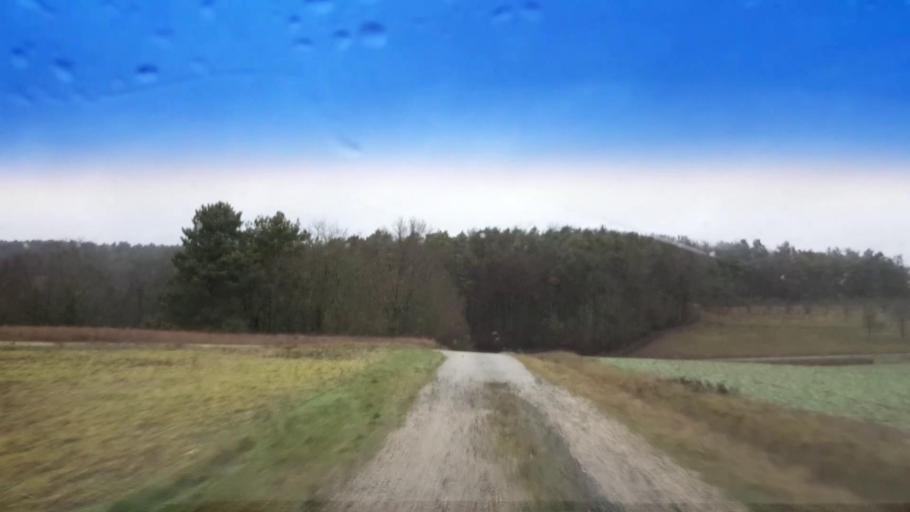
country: DE
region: Bavaria
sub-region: Upper Franconia
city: Lauter
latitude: 49.9522
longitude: 10.7680
